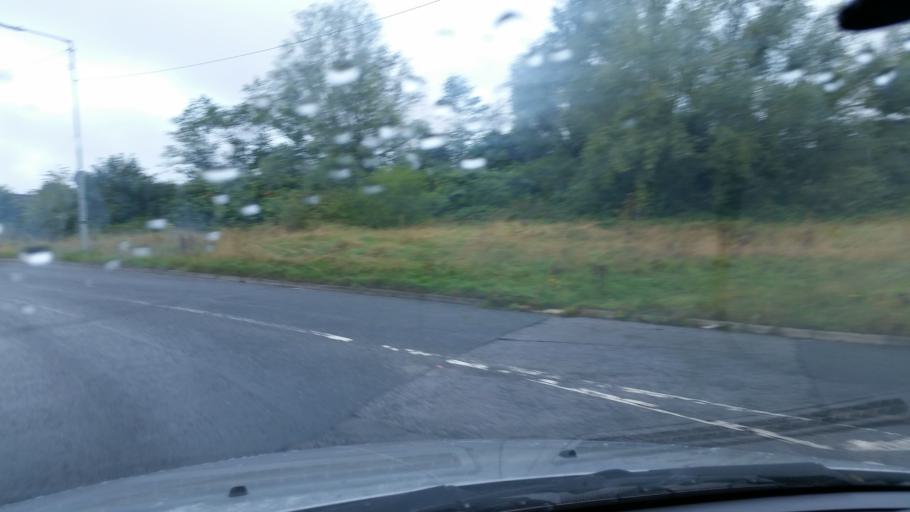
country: IE
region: Leinster
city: Ballymun
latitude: 53.4031
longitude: -6.2822
